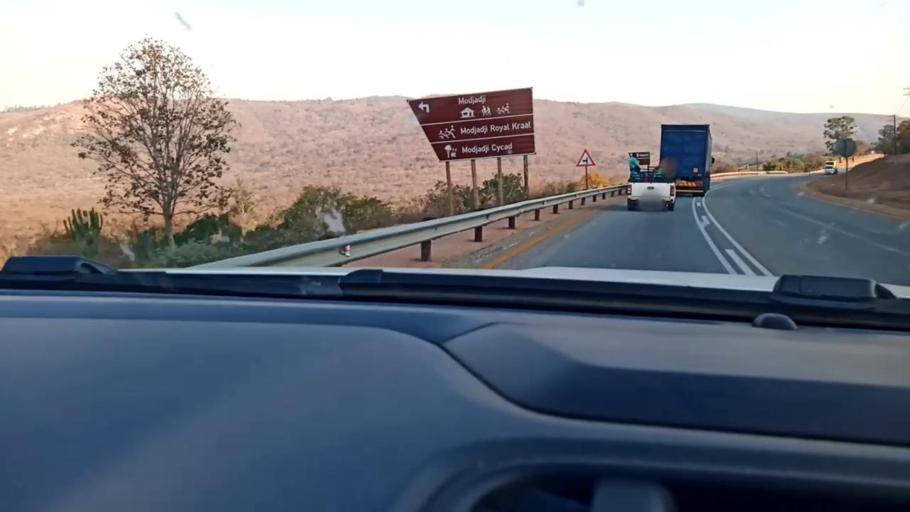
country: ZA
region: Limpopo
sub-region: Mopani District Municipality
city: Ga-Kgapane
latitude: -23.6508
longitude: 30.1721
